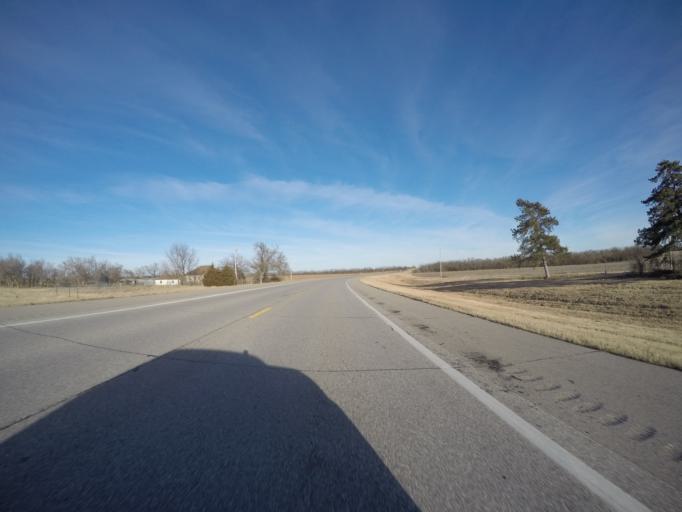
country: US
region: Kansas
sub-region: Marion County
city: Peabody
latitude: 38.1746
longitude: -97.1889
